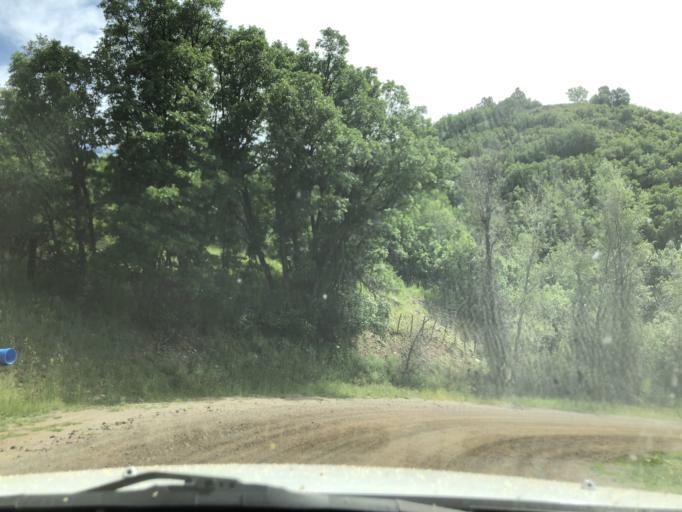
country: US
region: Colorado
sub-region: Delta County
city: Paonia
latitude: 38.9946
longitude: -107.3524
